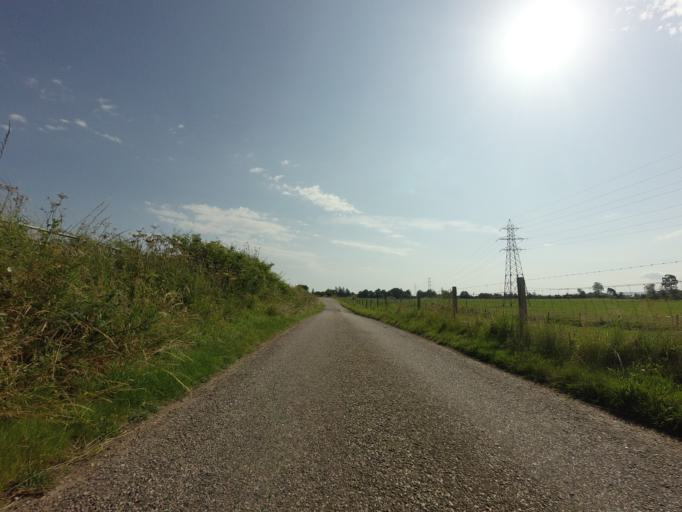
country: GB
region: Scotland
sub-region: Highland
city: Alness
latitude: 57.7052
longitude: -4.2495
